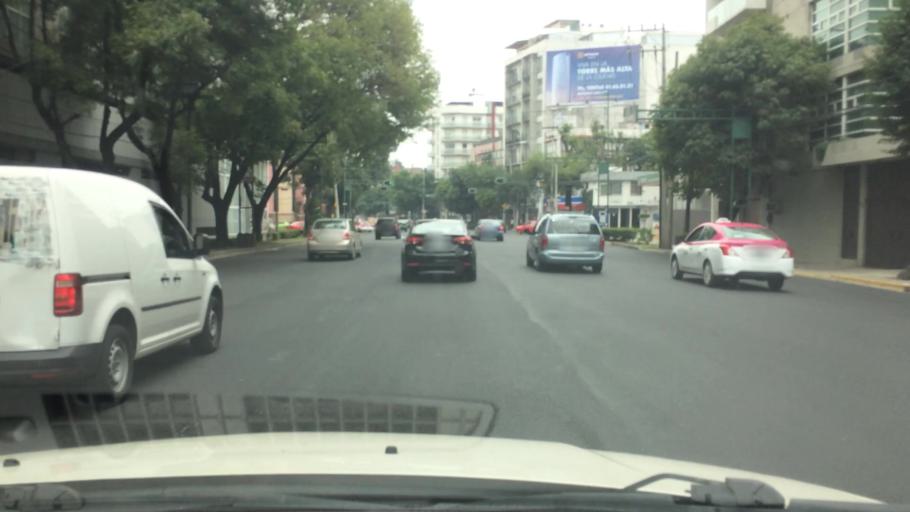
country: MX
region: Mexico City
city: Coyoacan
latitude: 19.3626
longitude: -99.1577
